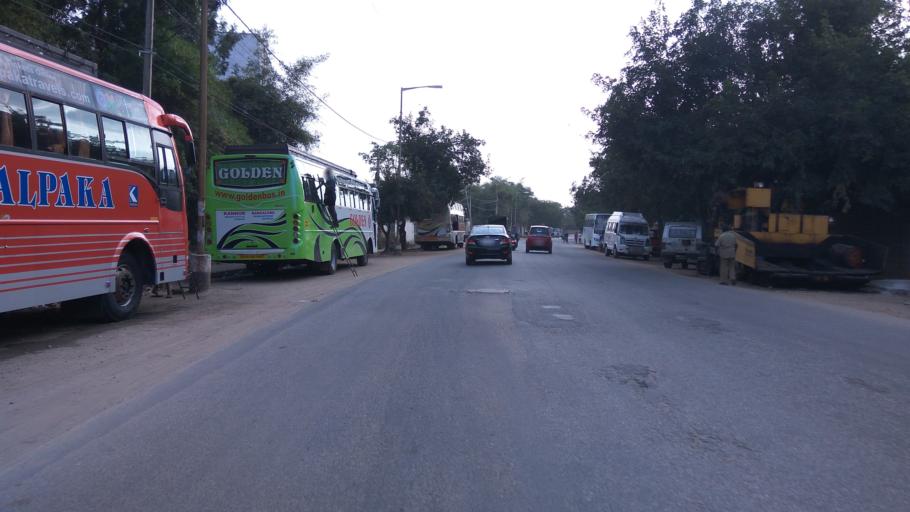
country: IN
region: Karnataka
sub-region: Bangalore Urban
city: Bangalore
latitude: 12.9670
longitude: 77.6932
